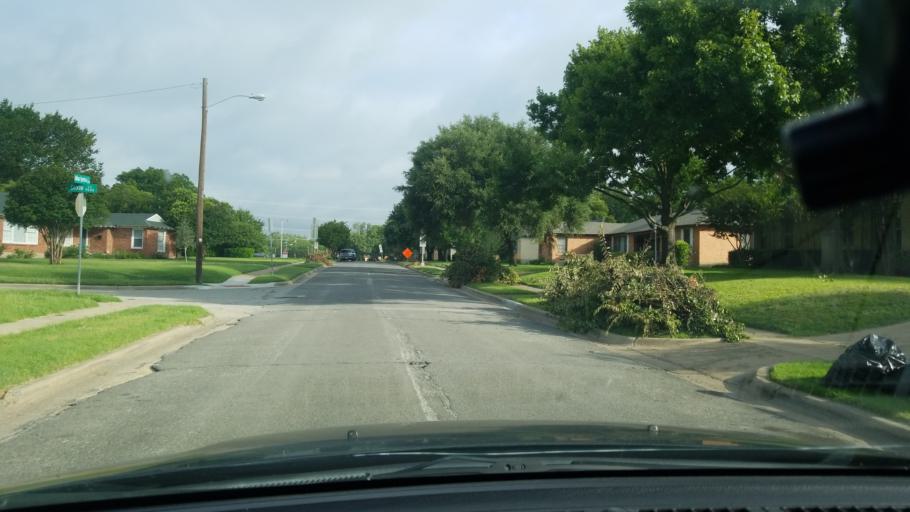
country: US
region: Texas
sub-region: Dallas County
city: Highland Park
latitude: 32.8250
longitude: -96.6914
